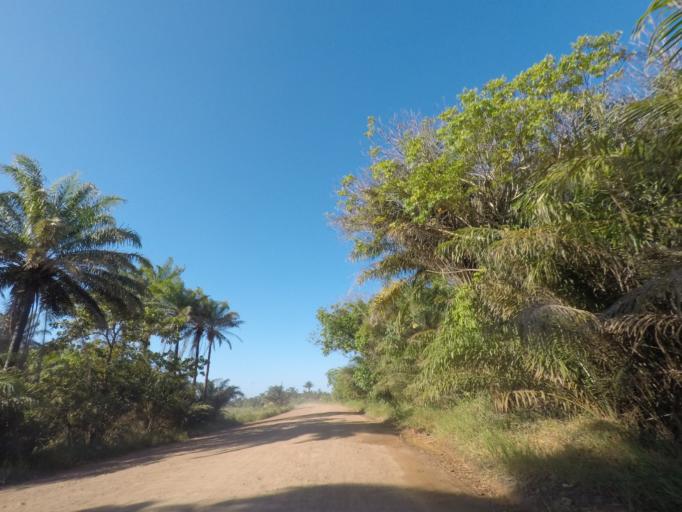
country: BR
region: Bahia
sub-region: Marau
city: Marau
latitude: -14.0499
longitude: -38.9545
